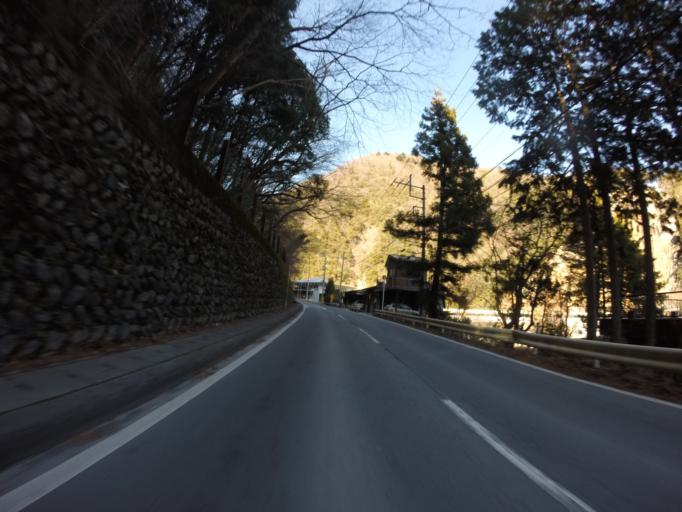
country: JP
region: Yamanashi
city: Ryuo
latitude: 35.4117
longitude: 138.3639
